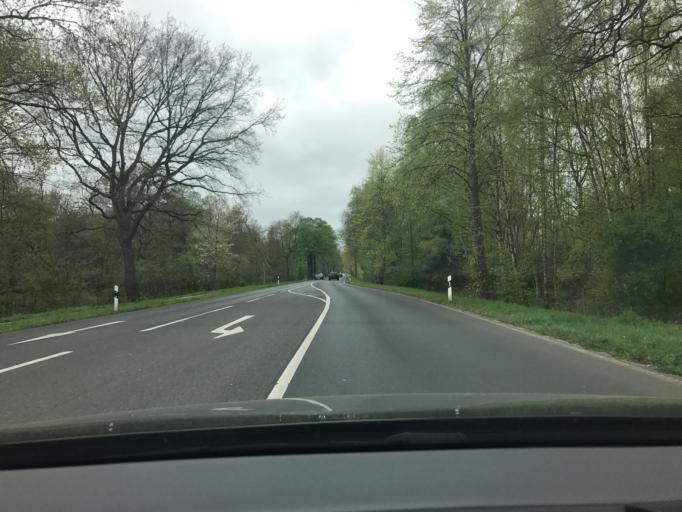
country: DE
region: North Rhine-Westphalia
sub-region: Regierungsbezirk Dusseldorf
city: Kaarst
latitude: 51.2283
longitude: 6.5774
